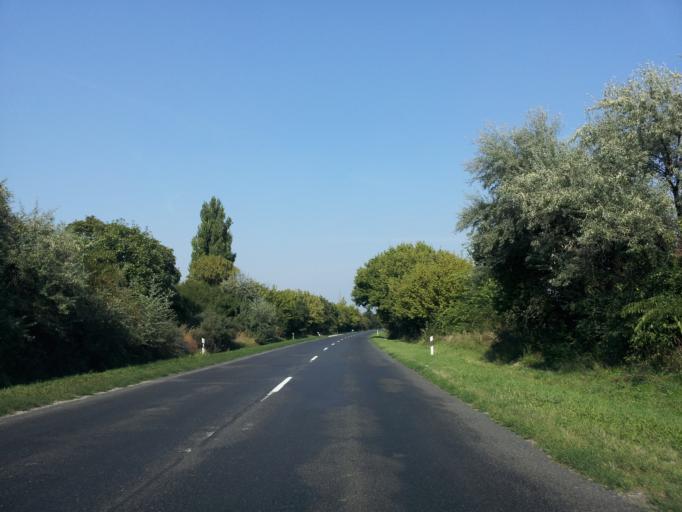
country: HU
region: Fejer
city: Lepseny
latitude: 46.9633
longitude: 18.1953
